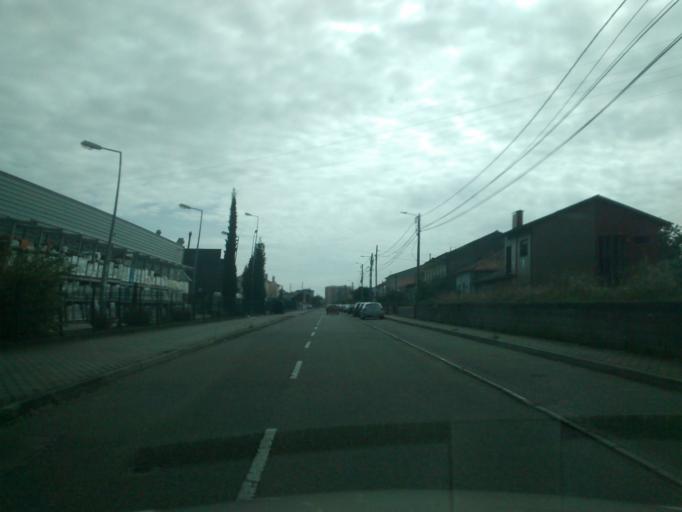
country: PT
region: Aveiro
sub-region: Aveiro
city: Aveiro
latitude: 40.6584
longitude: -8.6166
